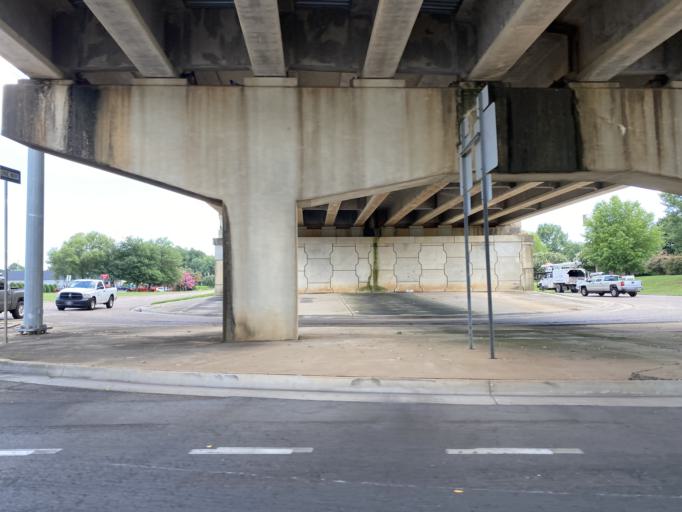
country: US
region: Alabama
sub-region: Madison County
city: Redstone Arsenal
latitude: 34.7570
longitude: -86.6725
